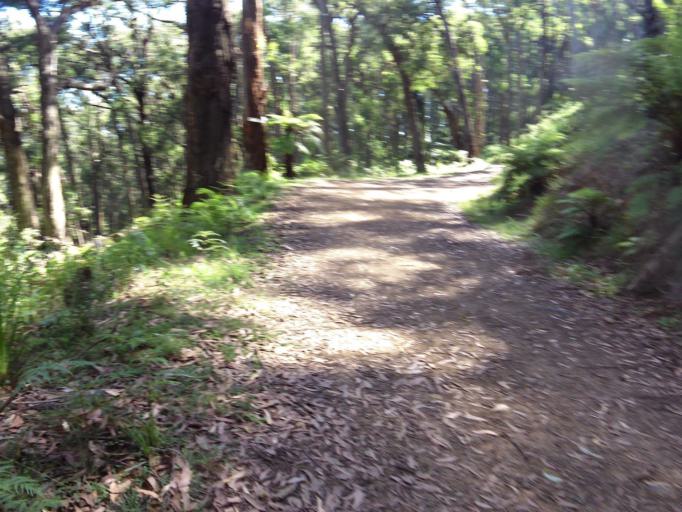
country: AU
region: Victoria
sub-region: Yarra Ranges
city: Mount Dandenong
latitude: -37.8404
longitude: 145.3438
